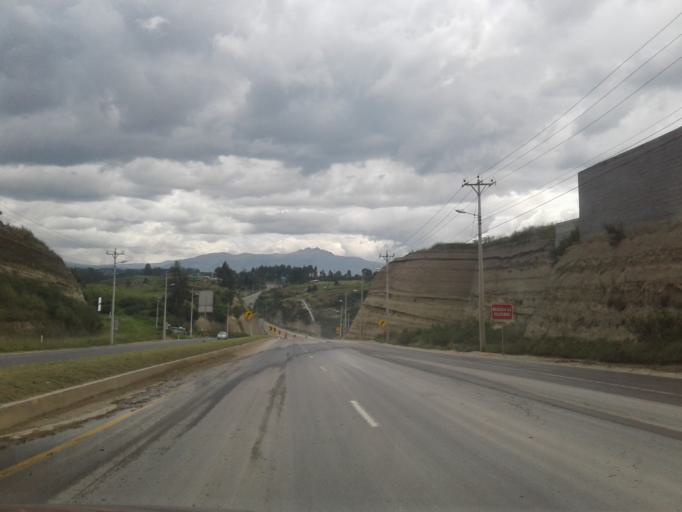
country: EC
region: Pichincha
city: Sangolqui
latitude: -0.3006
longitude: -78.3595
